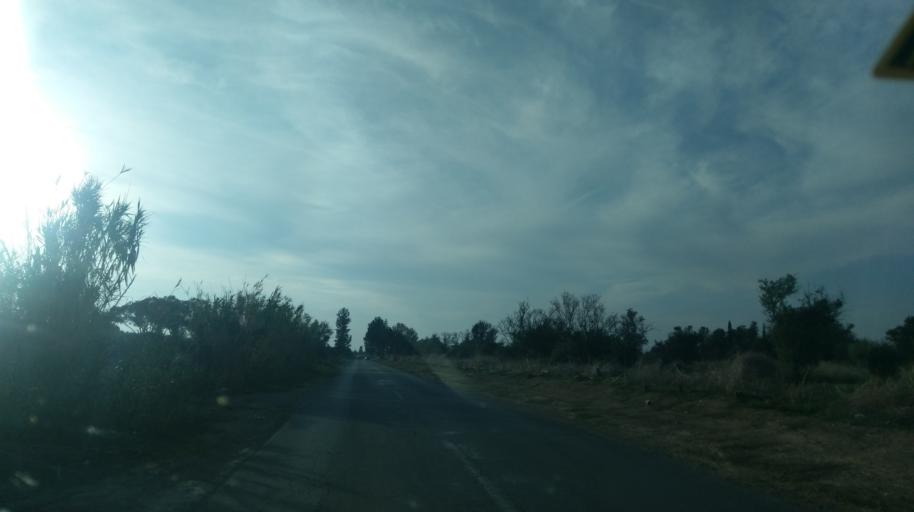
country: CY
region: Larnaka
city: Pergamos
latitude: 35.1055
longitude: 33.6984
